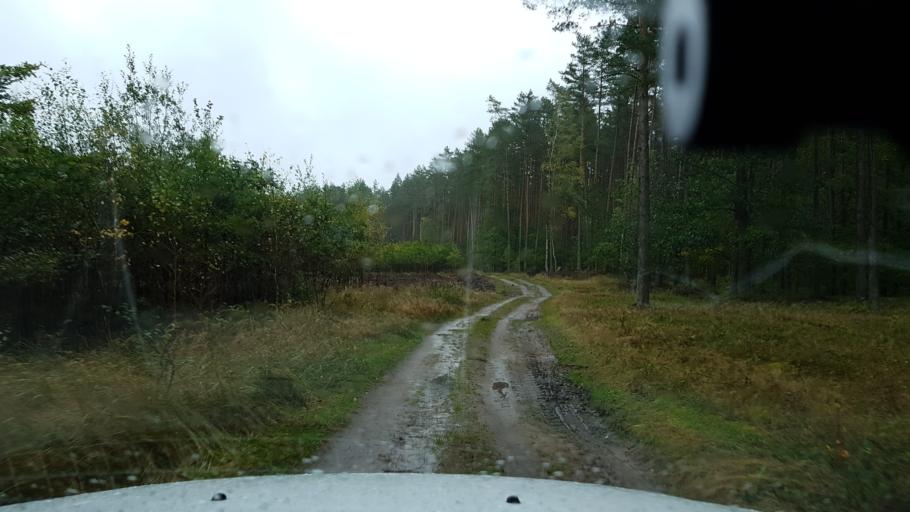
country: PL
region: West Pomeranian Voivodeship
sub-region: Powiat goleniowski
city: Przybiernow
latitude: 53.7373
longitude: 14.7874
